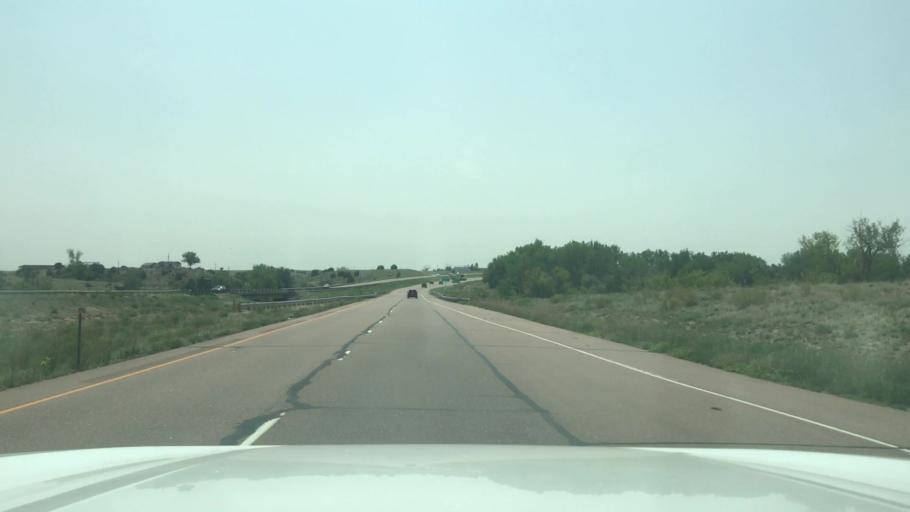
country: US
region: Colorado
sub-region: Pueblo County
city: Pueblo
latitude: 38.1228
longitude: -104.6713
